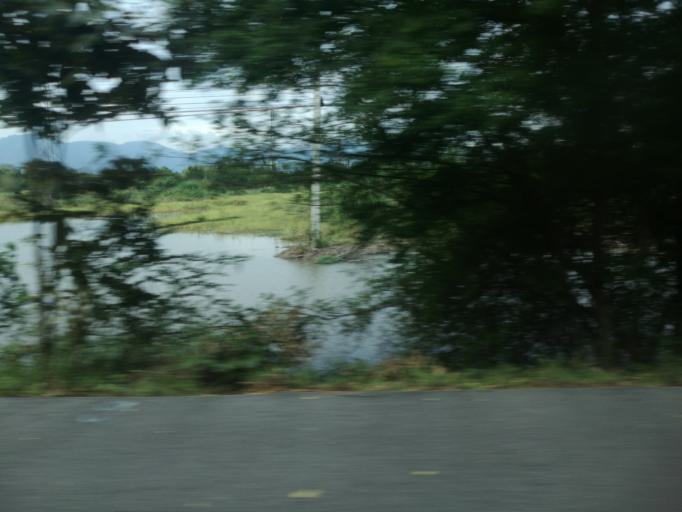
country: TH
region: Phetchaburi
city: Cha-am
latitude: 12.7781
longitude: 99.9371
